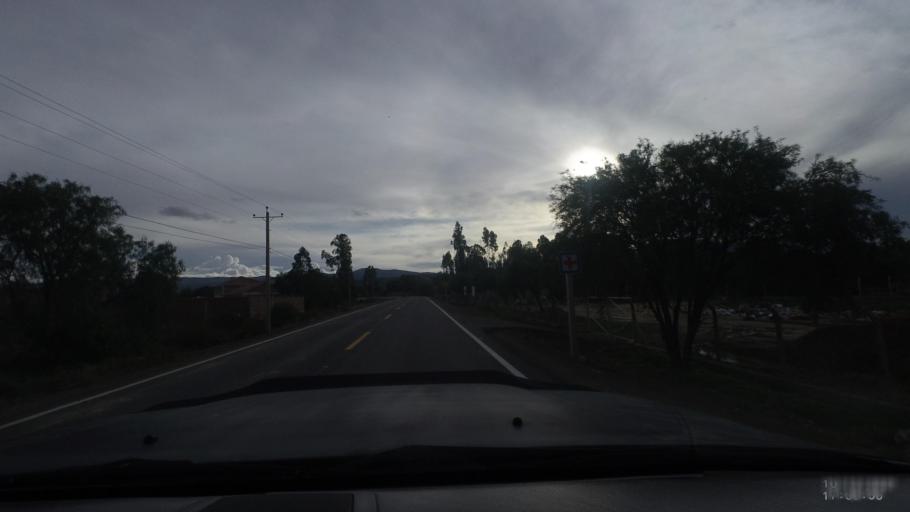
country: BO
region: Cochabamba
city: Tarata
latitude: -17.5822
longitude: -66.0176
